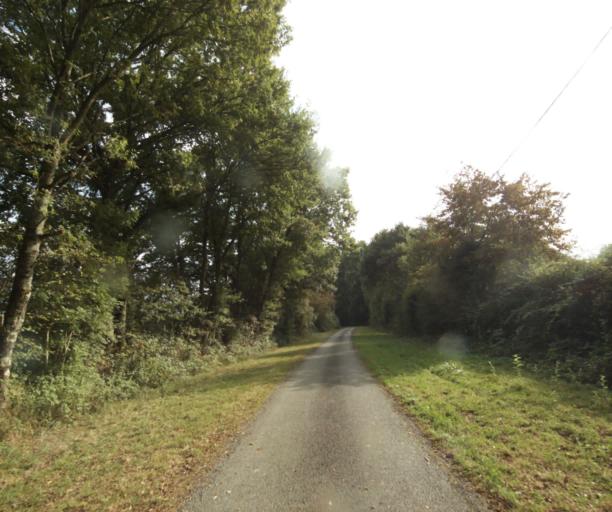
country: FR
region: Bourgogne
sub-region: Departement de Saone-et-Loire
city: Palinges
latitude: 46.5222
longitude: 4.2462
